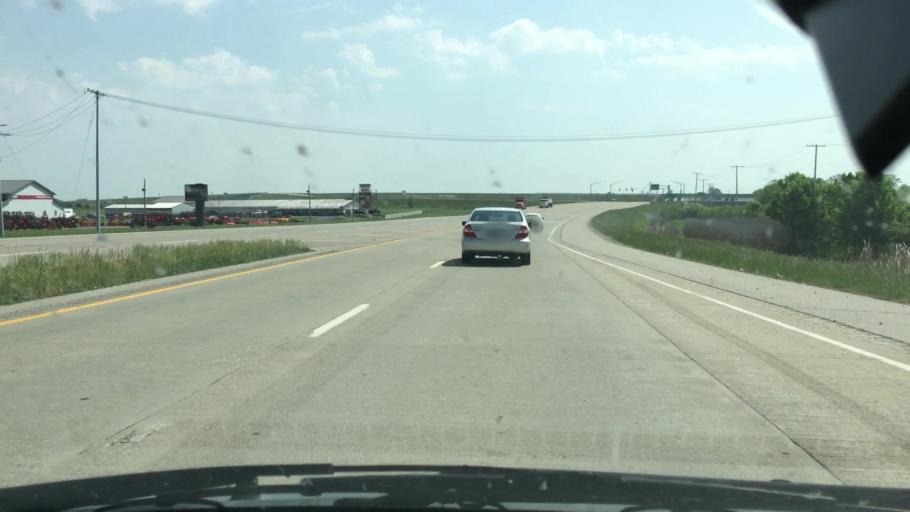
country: US
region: Indiana
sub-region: Daviess County
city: Washington
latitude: 38.6542
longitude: -87.1291
